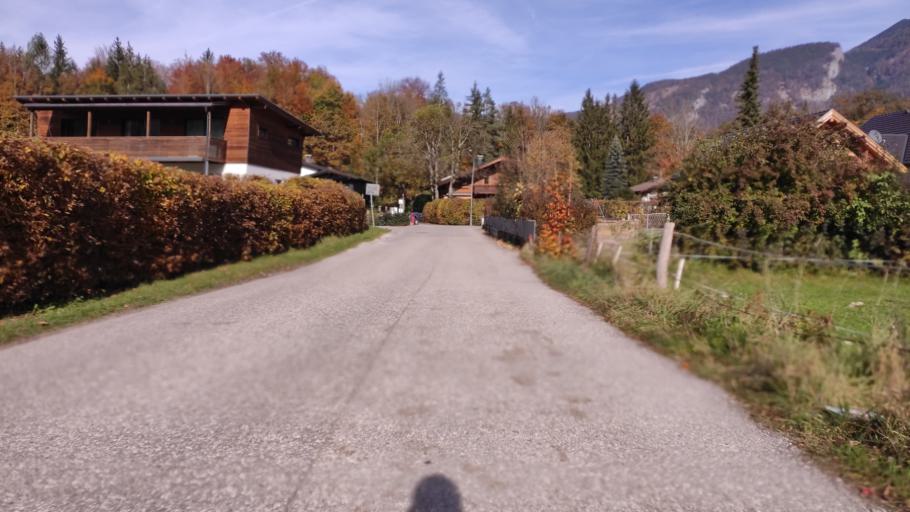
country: AT
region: Salzburg
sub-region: Politischer Bezirk Salzburg-Umgebung
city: Strobl
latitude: 47.7177
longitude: 13.5265
